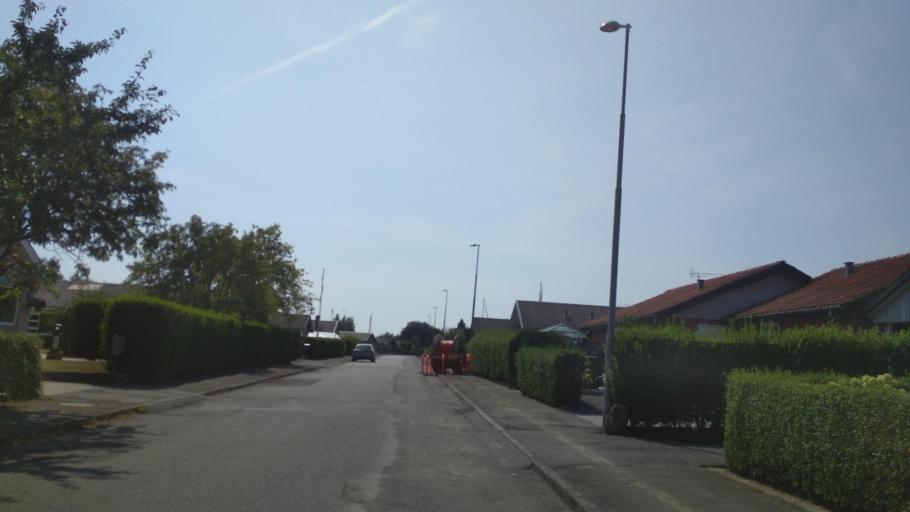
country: DK
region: Capital Region
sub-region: Bornholm Kommune
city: Akirkeby
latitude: 55.0694
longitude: 14.9285
